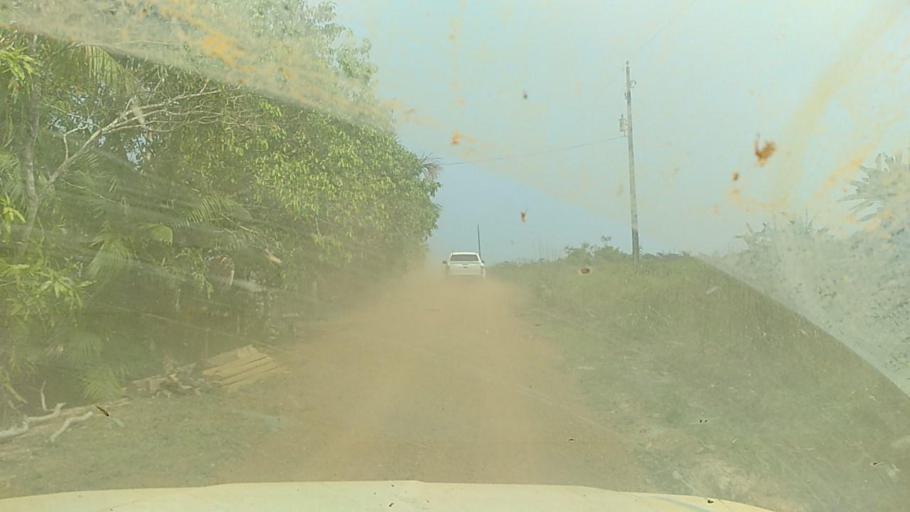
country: BR
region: Rondonia
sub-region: Porto Velho
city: Porto Velho
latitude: -8.9792
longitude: -64.3812
